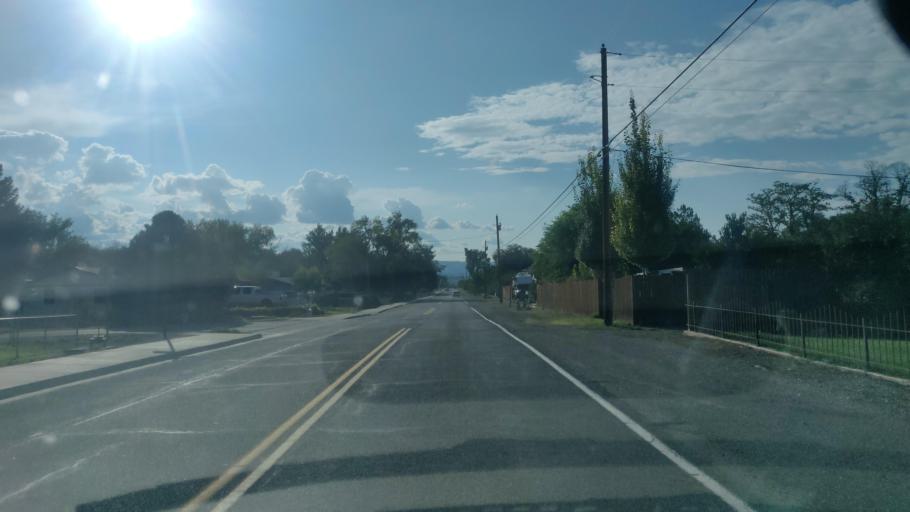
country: US
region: Colorado
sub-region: Mesa County
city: Orchard Mesa
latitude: 39.0340
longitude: -108.5093
